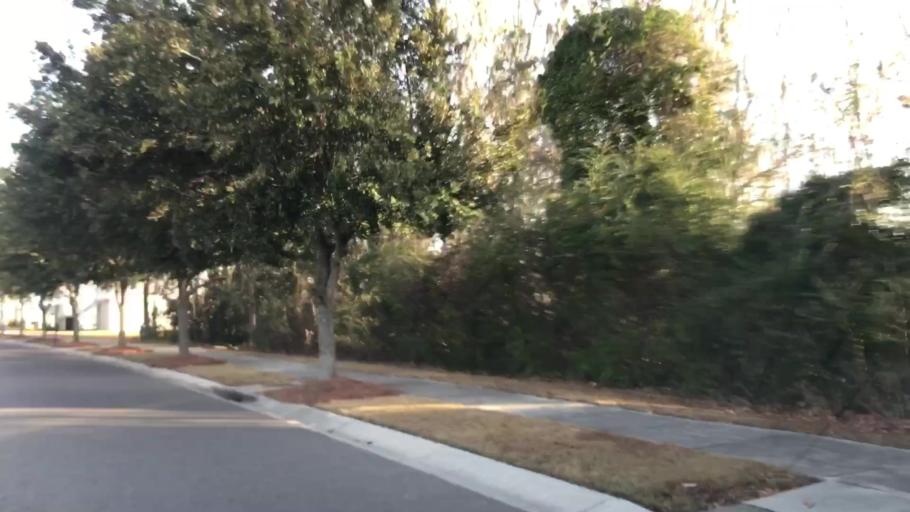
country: US
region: South Carolina
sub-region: Charleston County
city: Shell Point
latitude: 32.8084
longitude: -80.0515
